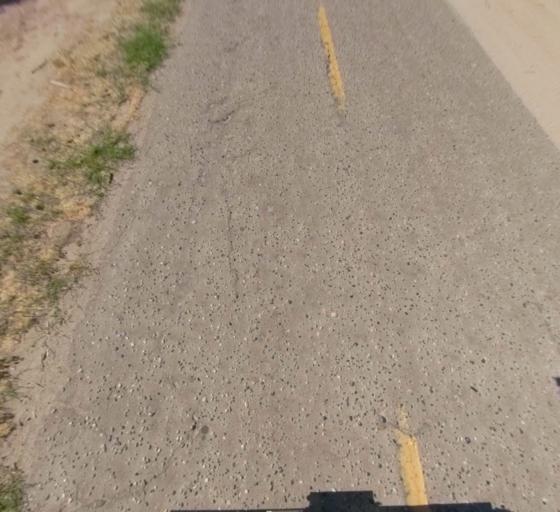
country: US
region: California
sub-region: Fresno County
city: Biola
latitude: 36.8307
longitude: -120.0247
